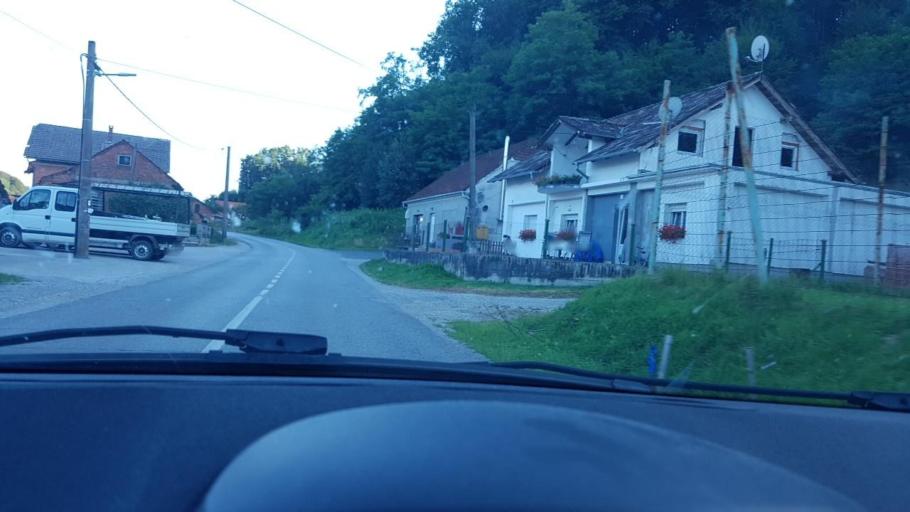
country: HR
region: Krapinsko-Zagorska
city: Bedekovcina
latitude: 46.0626
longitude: 16.0039
